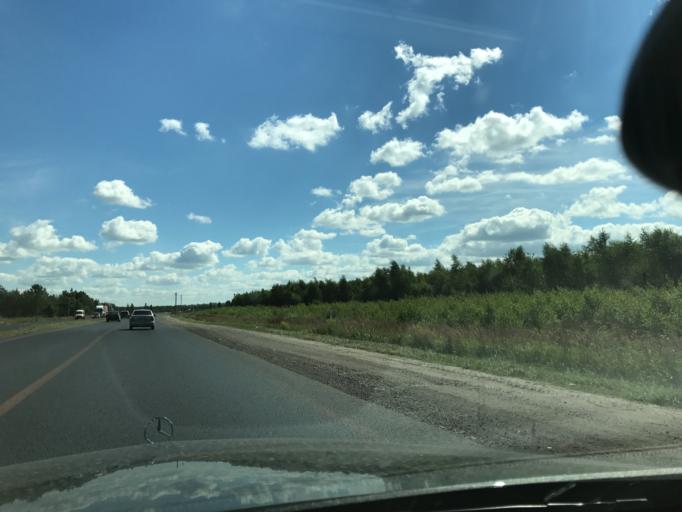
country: RU
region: Nizjnij Novgorod
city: Gorbatovka
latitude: 56.2309
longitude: 43.7440
